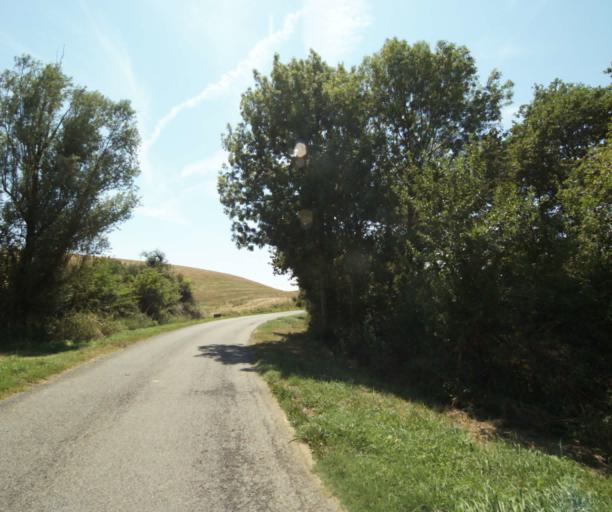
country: FR
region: Midi-Pyrenees
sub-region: Departement de l'Ariege
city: Lezat-sur-Leze
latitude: 43.2676
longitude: 1.3352
